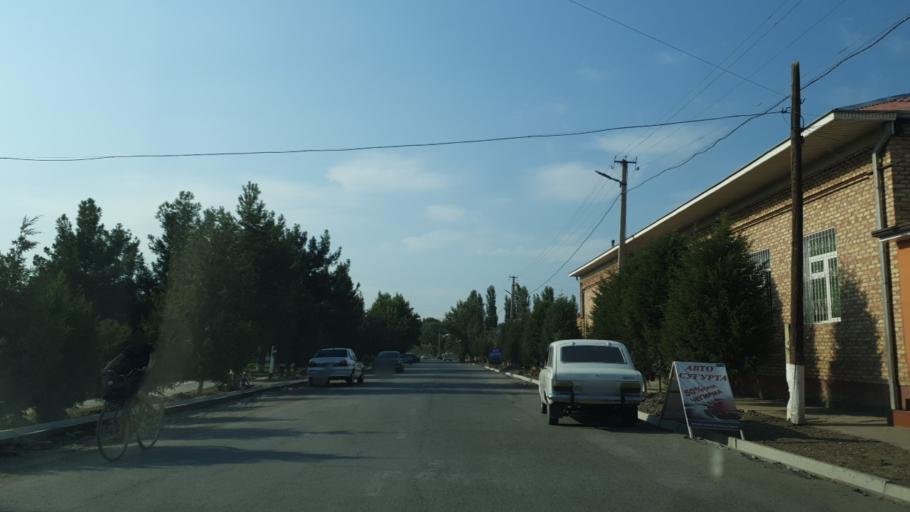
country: UZ
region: Fergana
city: Yaypan
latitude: 40.3748
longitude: 70.8124
